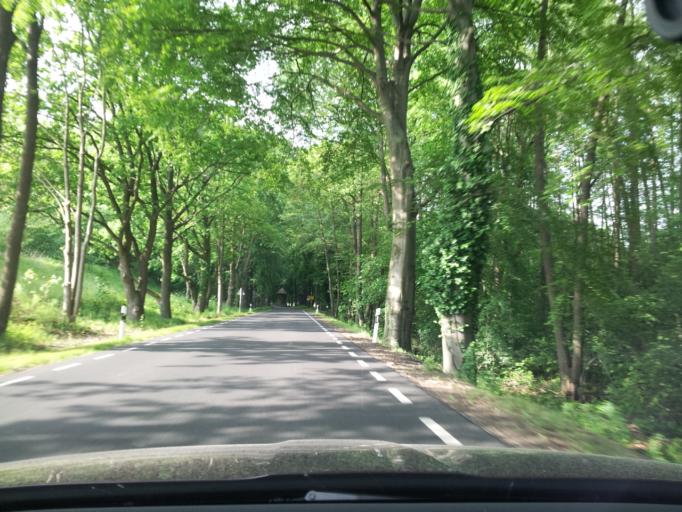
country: DE
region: Brandenburg
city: Werder
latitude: 52.3393
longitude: 12.9406
